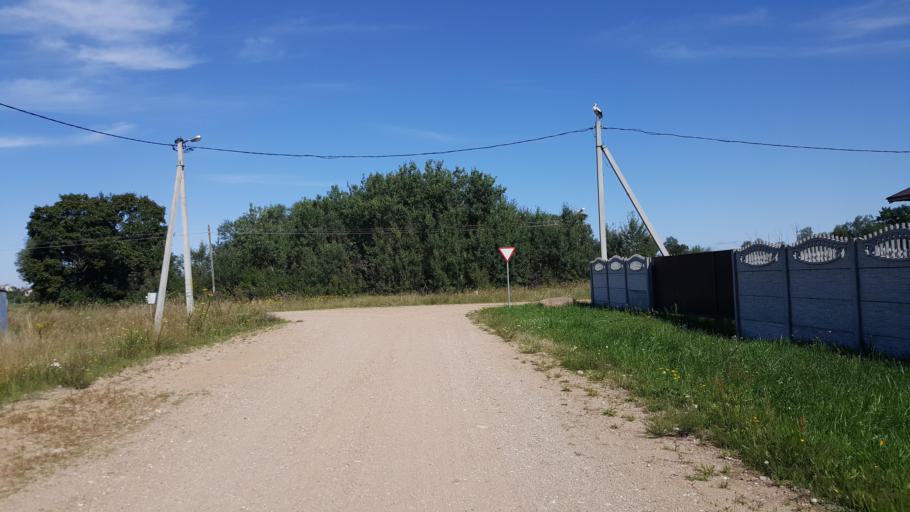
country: BY
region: Brest
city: Charnawchytsy
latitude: 52.2704
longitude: 23.7649
